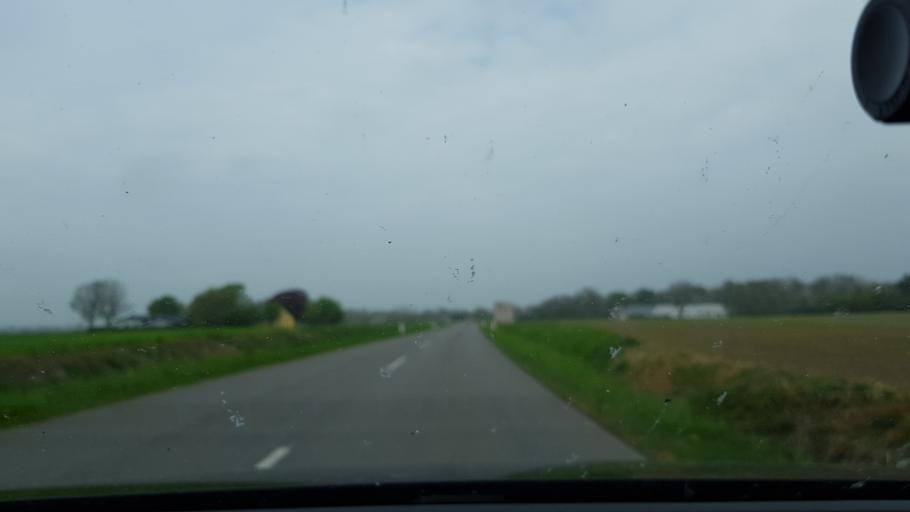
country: DK
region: Capital Region
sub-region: Bornholm Kommune
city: Nexo
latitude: 55.0202
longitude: 15.0967
